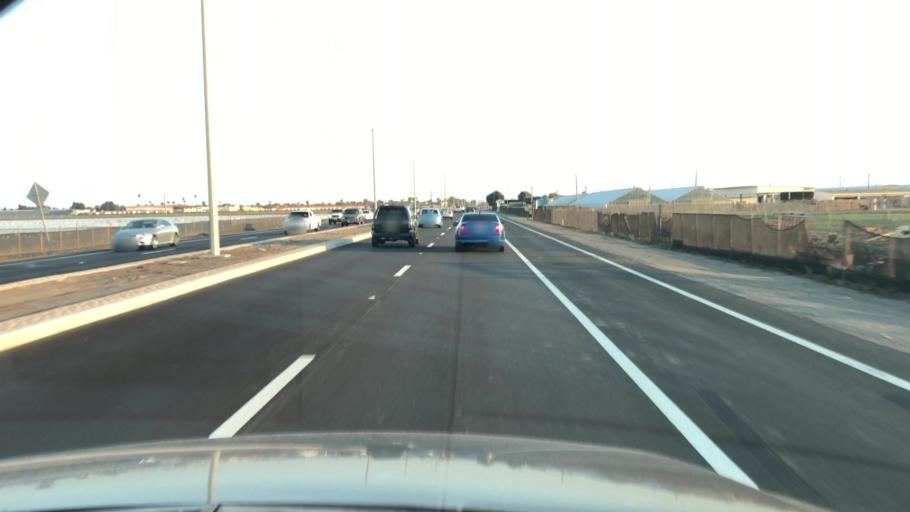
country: US
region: California
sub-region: Ventura County
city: Oxnard Shores
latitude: 34.2070
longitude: -119.2210
